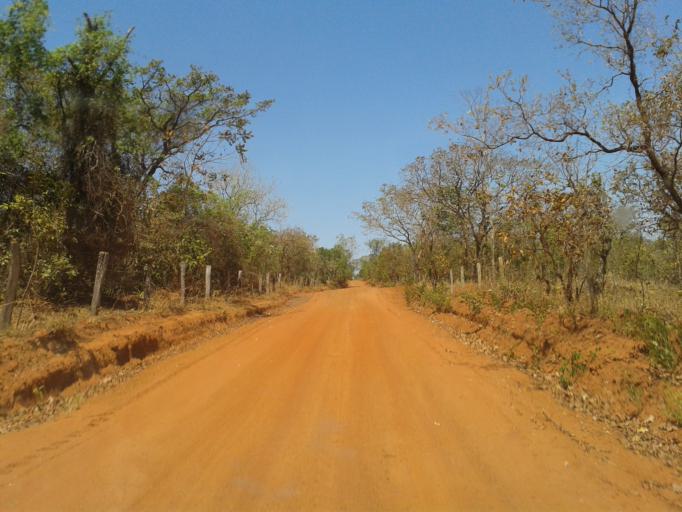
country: BR
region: Minas Gerais
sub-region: Ituiutaba
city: Ituiutaba
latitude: -19.0729
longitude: -49.3175
